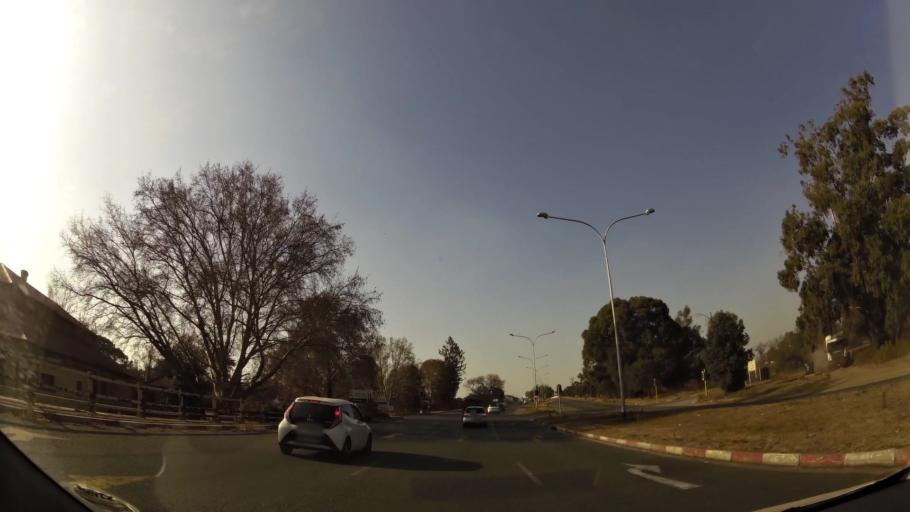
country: ZA
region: Gauteng
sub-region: West Rand District Municipality
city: Randfontein
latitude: -26.1619
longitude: 27.7137
